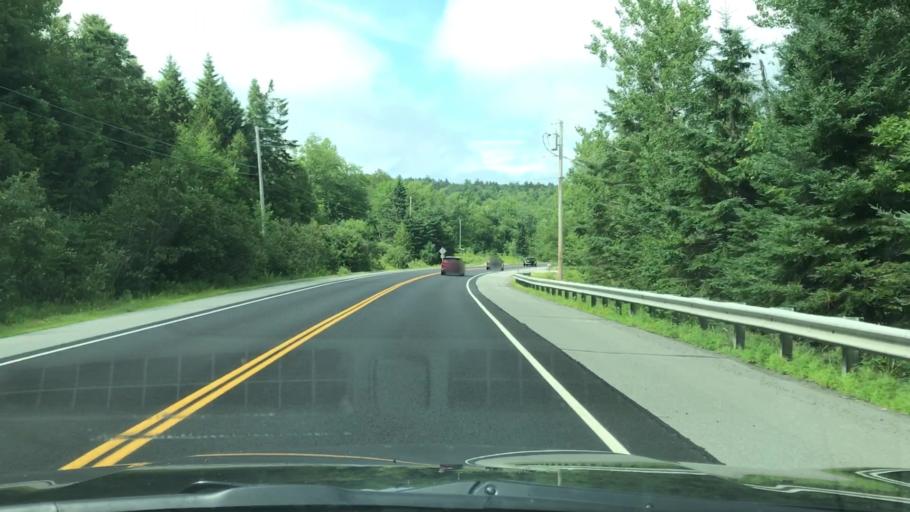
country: US
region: Maine
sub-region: Hancock County
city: Bucksport
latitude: 44.5529
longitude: -68.8101
